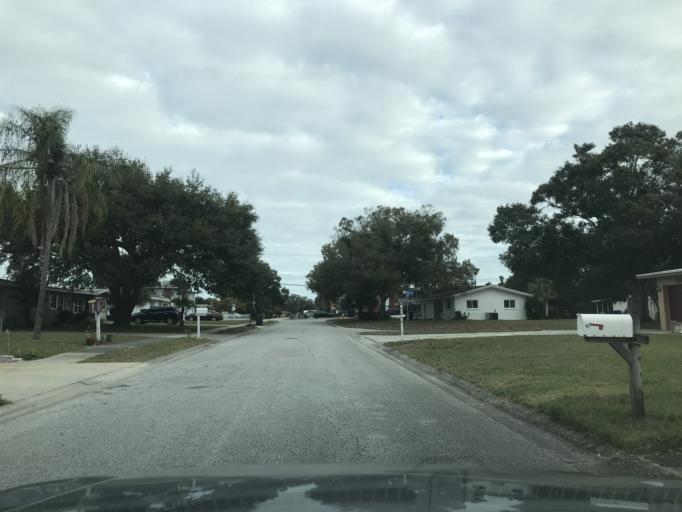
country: US
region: Florida
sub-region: Pinellas County
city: Largo
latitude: 27.9306
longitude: -82.7859
